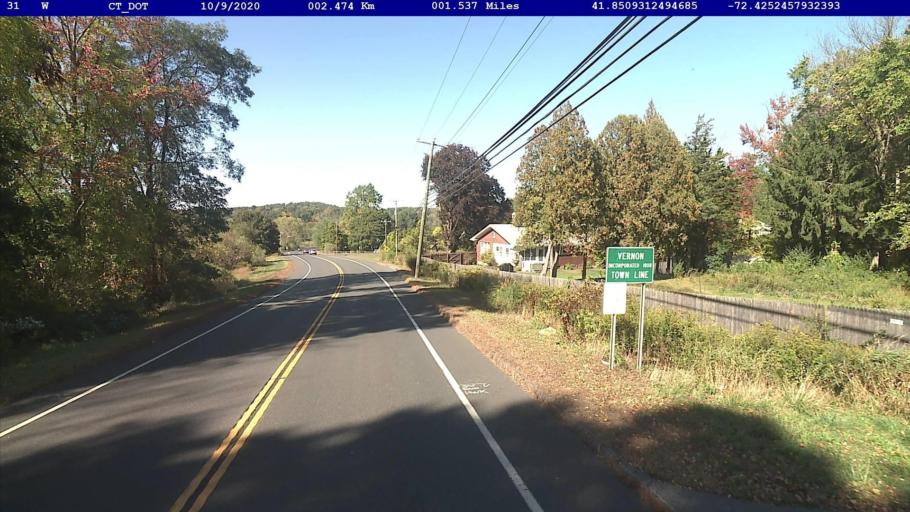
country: US
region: Connecticut
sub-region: Tolland County
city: Rockville
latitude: 41.8509
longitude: -72.4253
